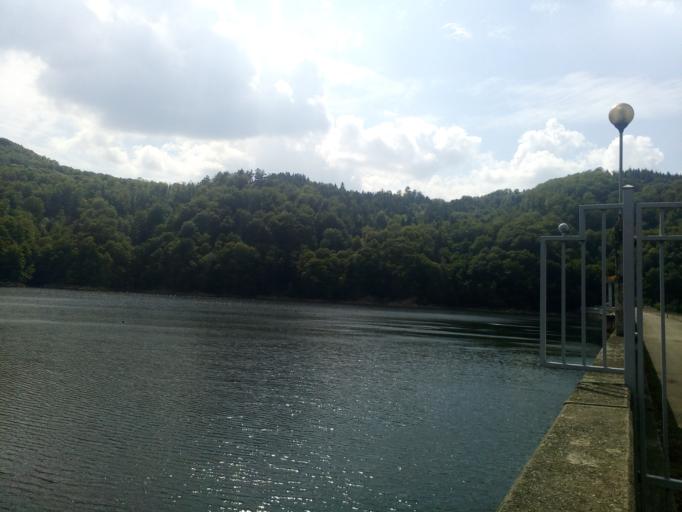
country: PL
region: Lesser Poland Voivodeship
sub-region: Powiat nowosadecki
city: Lososina Dolna
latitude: 49.7612
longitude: 20.6656
